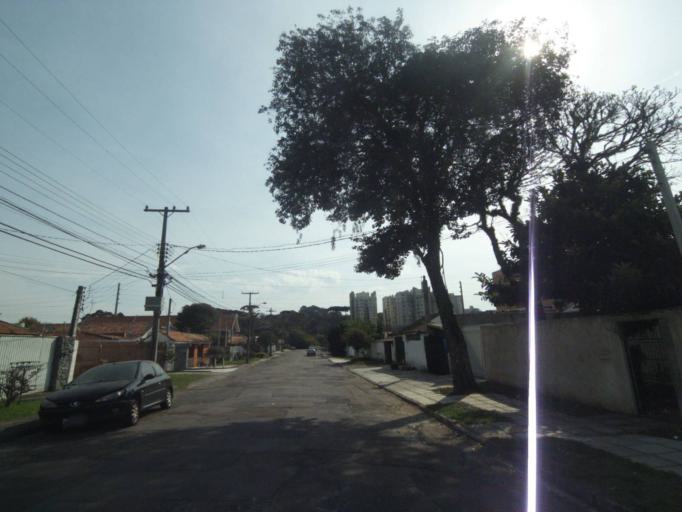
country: BR
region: Parana
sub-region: Curitiba
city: Curitiba
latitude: -25.4601
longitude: -49.3170
